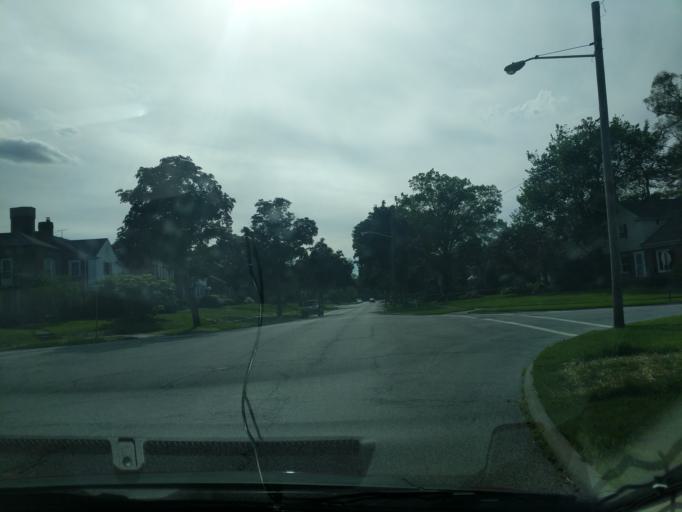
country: US
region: Ohio
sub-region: Cuyahoga County
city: University Heights
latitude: 41.4908
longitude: -81.5384
